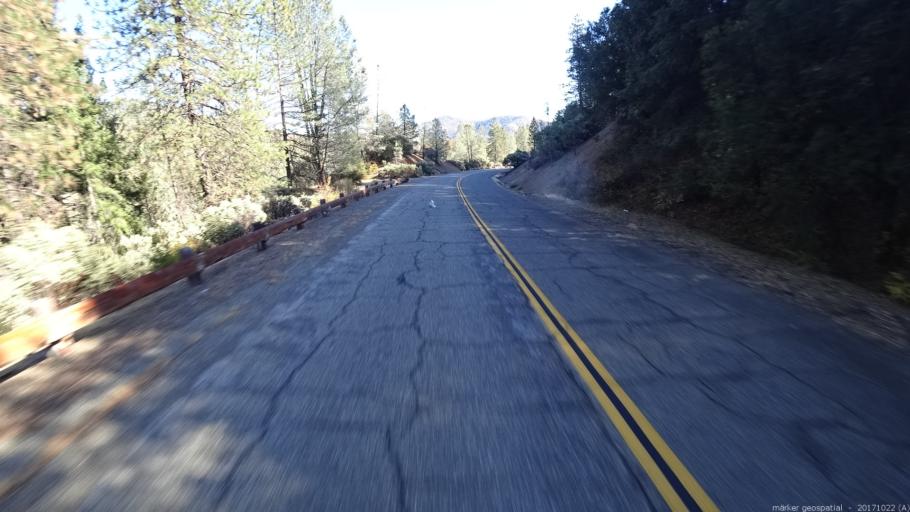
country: US
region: California
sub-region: Shasta County
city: Shasta Lake
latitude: 40.8626
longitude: -122.3592
